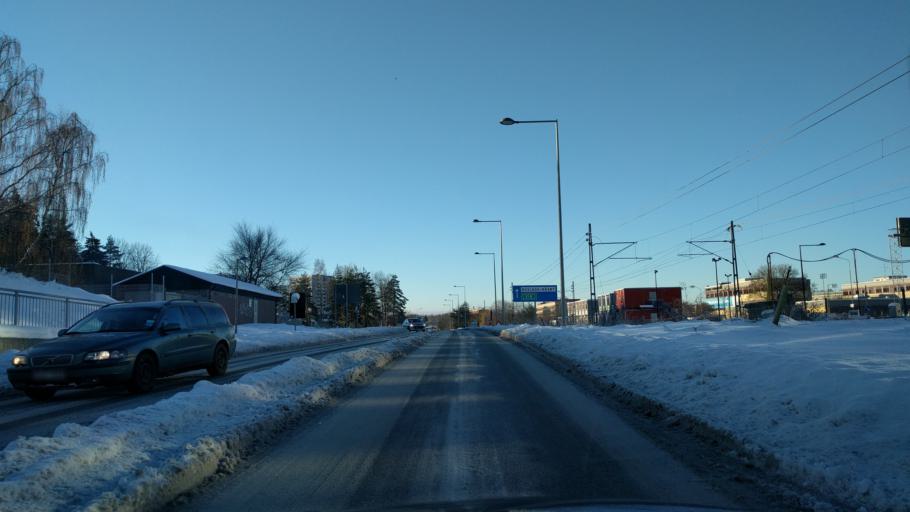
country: SE
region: Stockholm
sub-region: Taby Kommun
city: Taby
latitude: 59.4423
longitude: 18.0706
